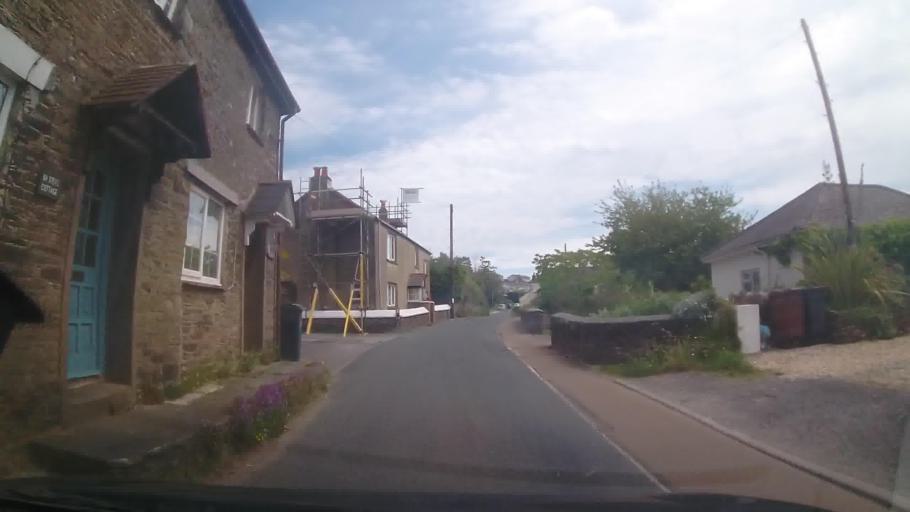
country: GB
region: England
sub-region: Devon
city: Kingsbridge
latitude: 50.2704
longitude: -3.7508
